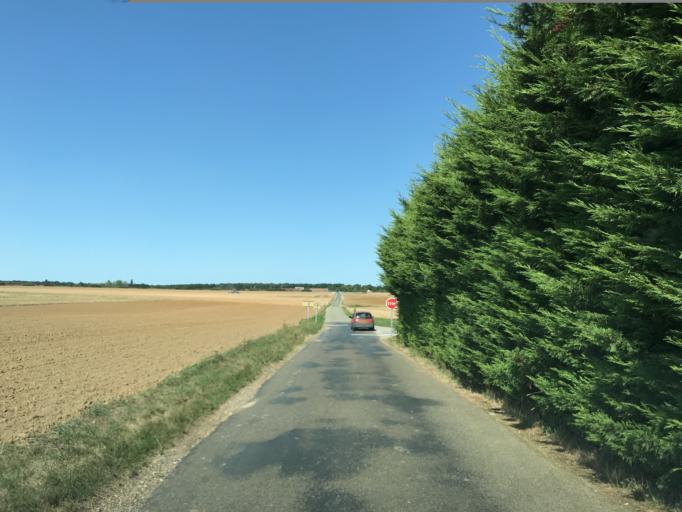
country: FR
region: Haute-Normandie
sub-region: Departement de l'Eure
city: Houlbec-Cocherel
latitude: 49.0645
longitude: 1.2689
